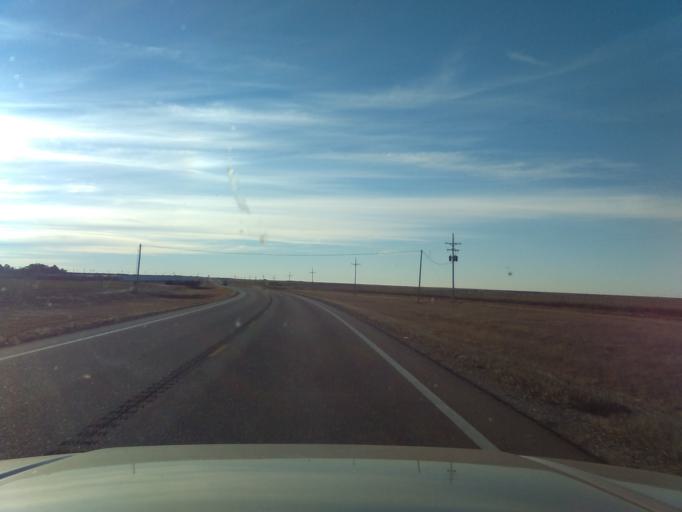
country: US
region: Kansas
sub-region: Thomas County
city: Colby
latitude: 39.4478
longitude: -100.8204
